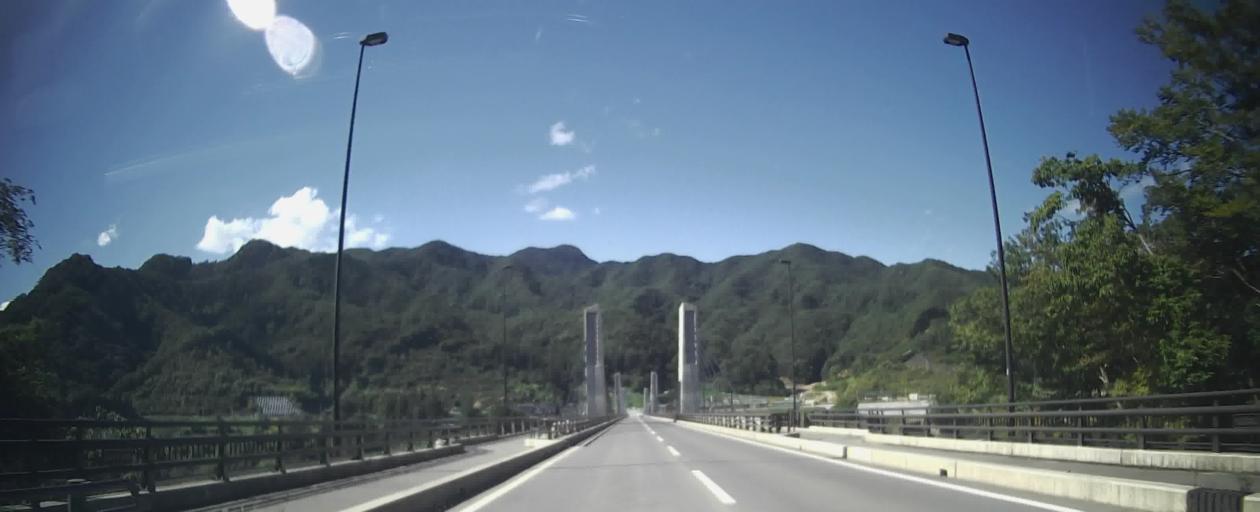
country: JP
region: Gunma
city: Nakanojomachi
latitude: 36.5514
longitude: 138.7074
